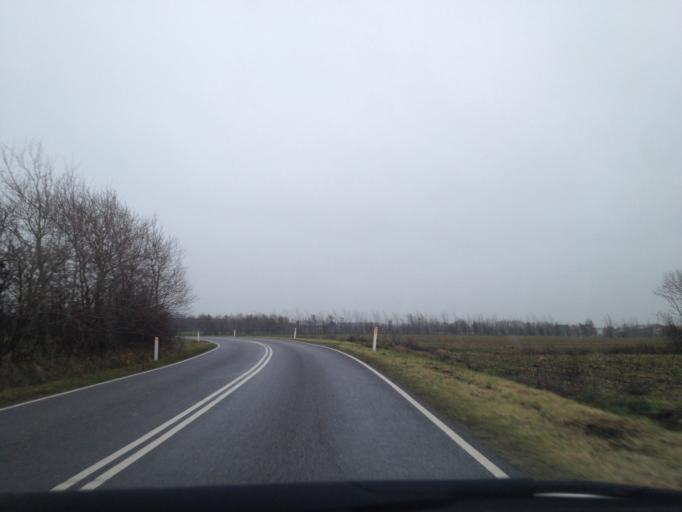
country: DK
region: South Denmark
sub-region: Tonder Kommune
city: Sherrebek
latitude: 55.0609
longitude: 8.7531
